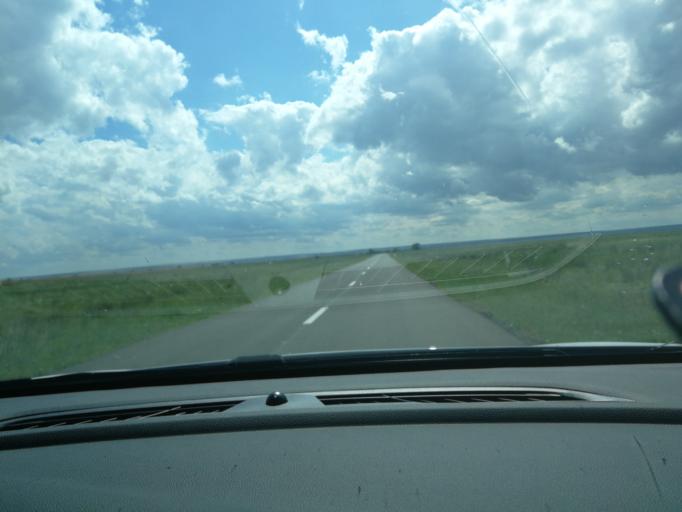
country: RO
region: Constanta
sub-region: Comuna Istria
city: Istria
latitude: 44.5432
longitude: 28.7651
